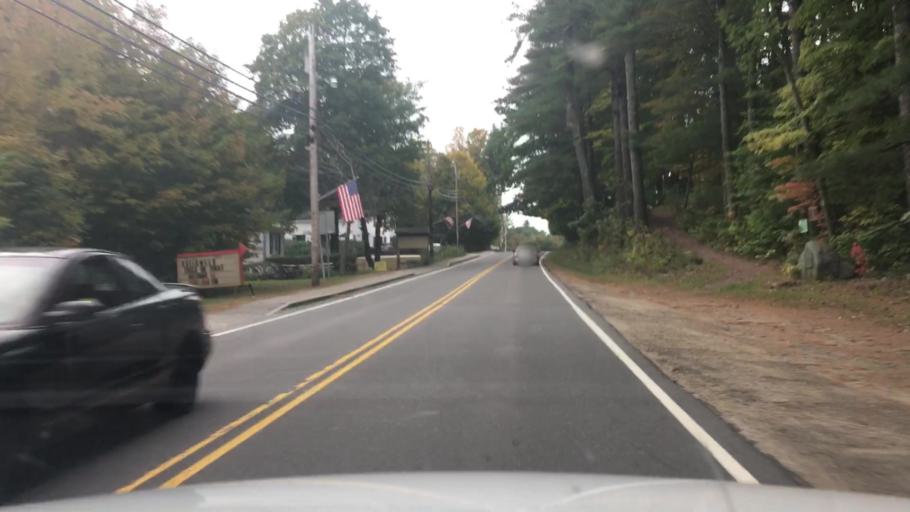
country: US
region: New Hampshire
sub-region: Strafford County
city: New Durham
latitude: 43.4674
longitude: -71.2311
